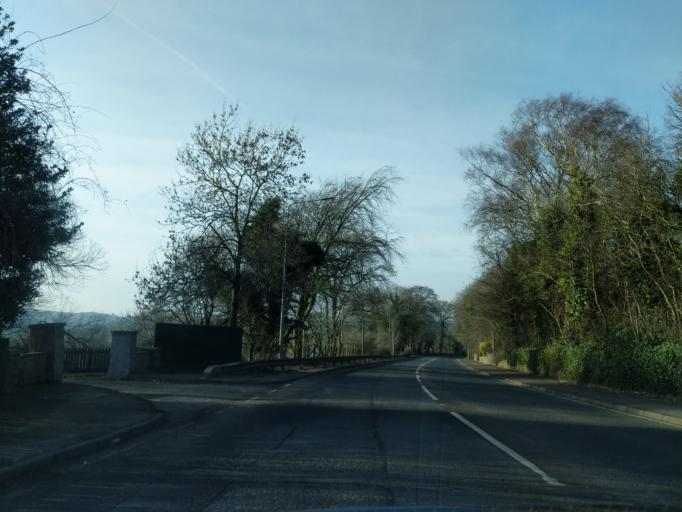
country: GB
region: Scotland
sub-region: South Lanarkshire
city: Lanark
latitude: 55.6759
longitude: -3.7935
